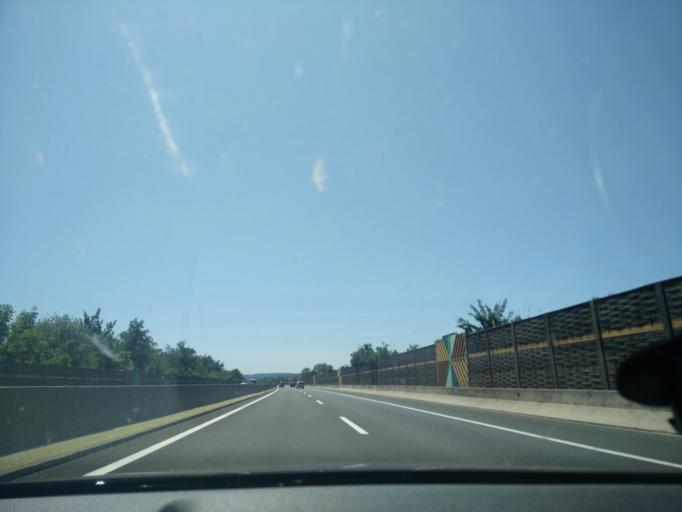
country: AT
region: Styria
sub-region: Politischer Bezirk Hartberg-Fuerstenfeld
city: Sankt Johann in der Haide
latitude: 47.2401
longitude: 15.9956
